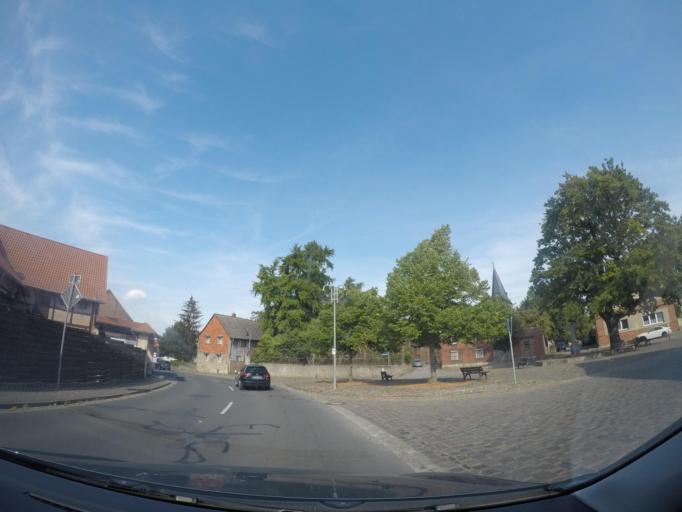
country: DE
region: Lower Saxony
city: Jerxheim
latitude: 52.0291
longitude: 10.8917
